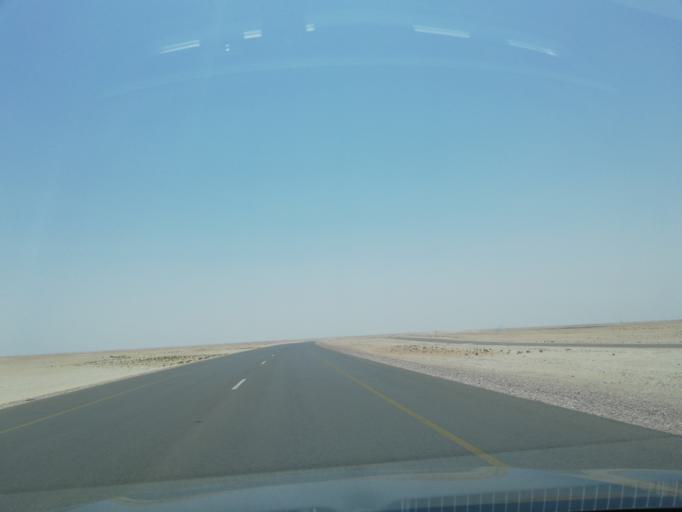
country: OM
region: Al Wusta
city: Hayma'
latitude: 19.7460
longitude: 56.0944
